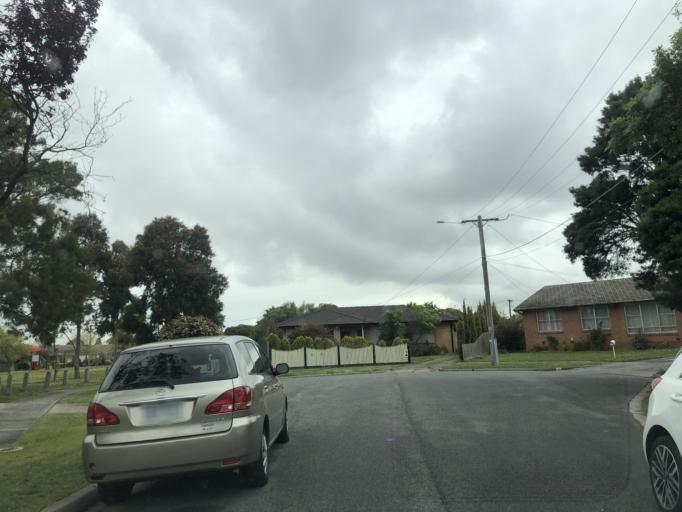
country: AU
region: Victoria
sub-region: Greater Dandenong
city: Dandenong North
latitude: -37.9600
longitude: 145.2088
